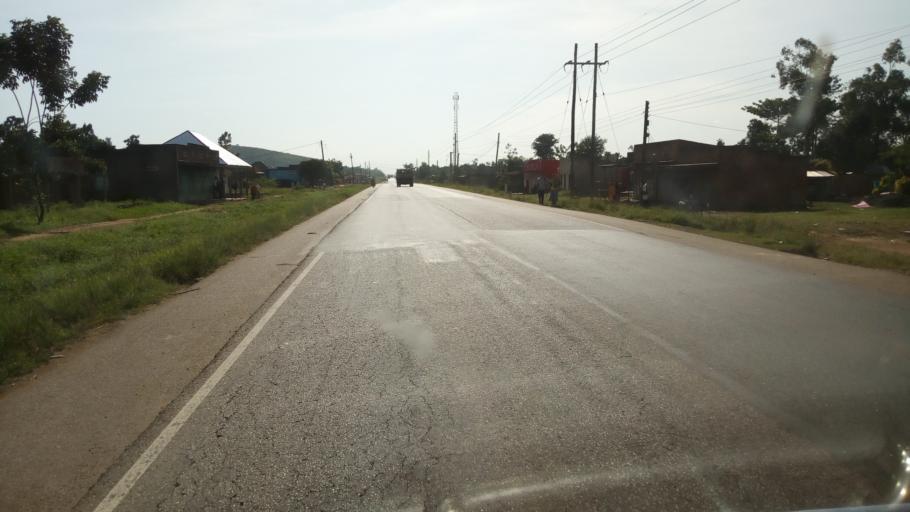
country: UG
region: Eastern Region
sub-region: Bugiri District
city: Bugiri
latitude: 0.5309
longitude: 33.8681
